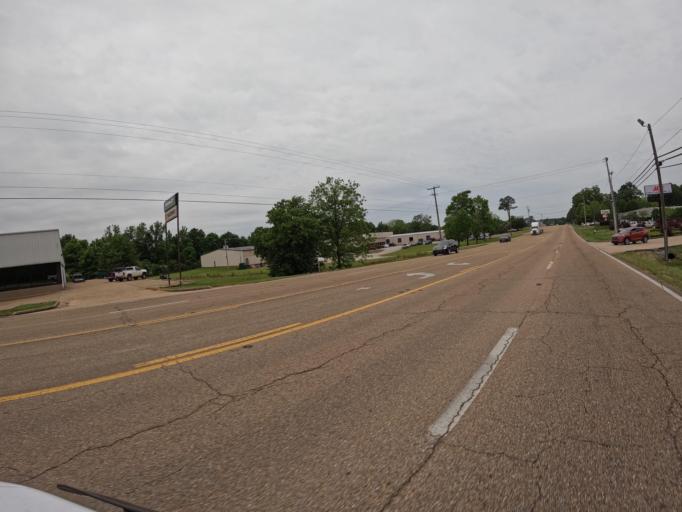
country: US
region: Mississippi
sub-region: Lee County
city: Tupelo
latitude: 34.2867
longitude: -88.7411
